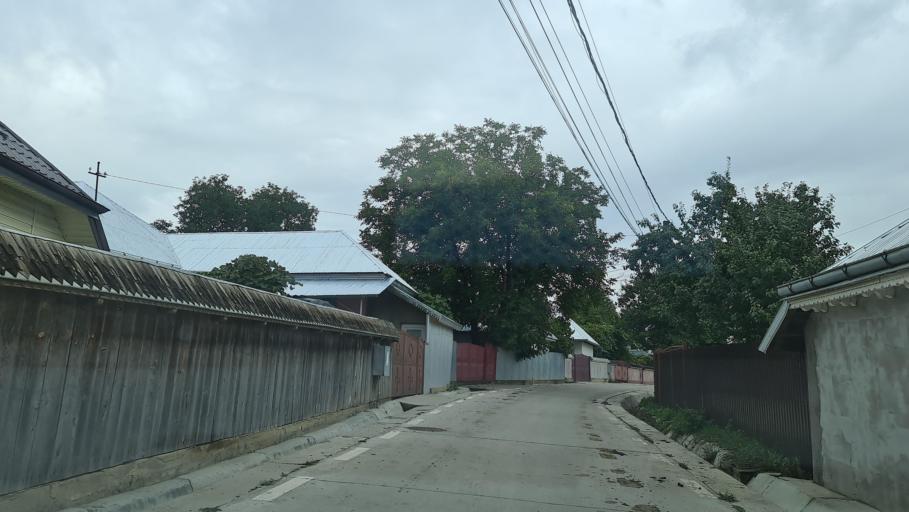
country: RO
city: Vanatori-Neamt
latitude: 47.2094
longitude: 26.3145
